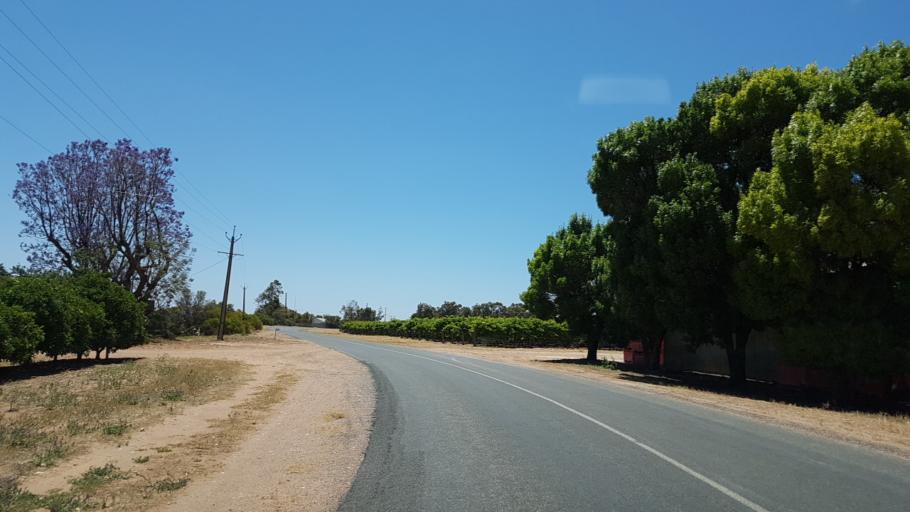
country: AU
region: South Australia
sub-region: Loxton Waikerie
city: Waikerie
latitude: -34.1744
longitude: 140.0303
